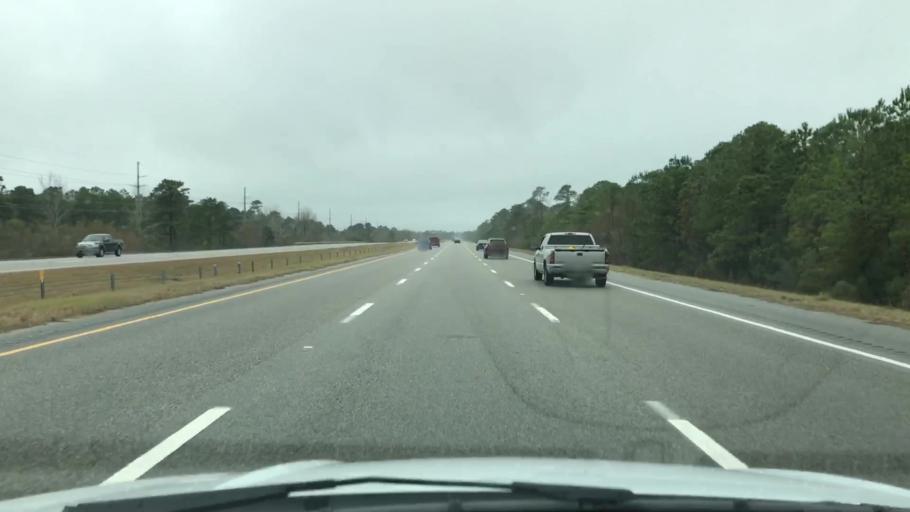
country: US
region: South Carolina
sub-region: Horry County
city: Forestbrook
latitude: 33.7472
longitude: -78.9125
